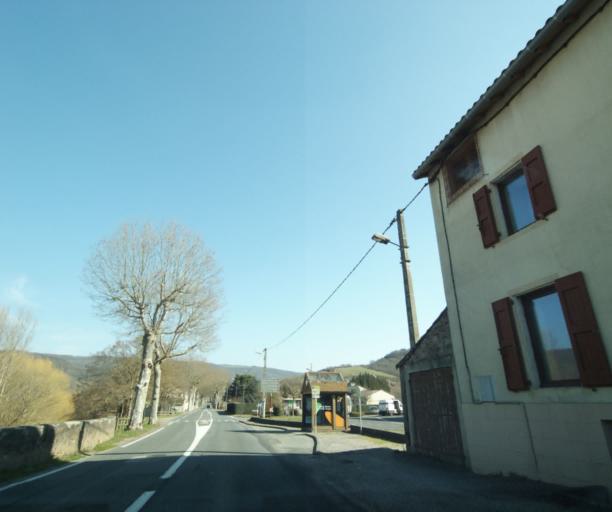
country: FR
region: Midi-Pyrenees
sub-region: Departement de l'Aveyron
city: Saint-Affrique
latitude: 43.9463
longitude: 2.8384
